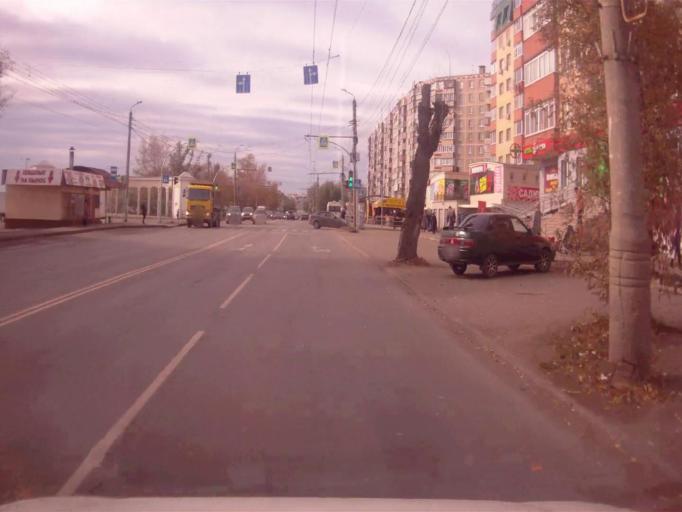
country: RU
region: Chelyabinsk
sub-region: Gorod Chelyabinsk
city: Chelyabinsk
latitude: 55.1134
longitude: 61.4588
